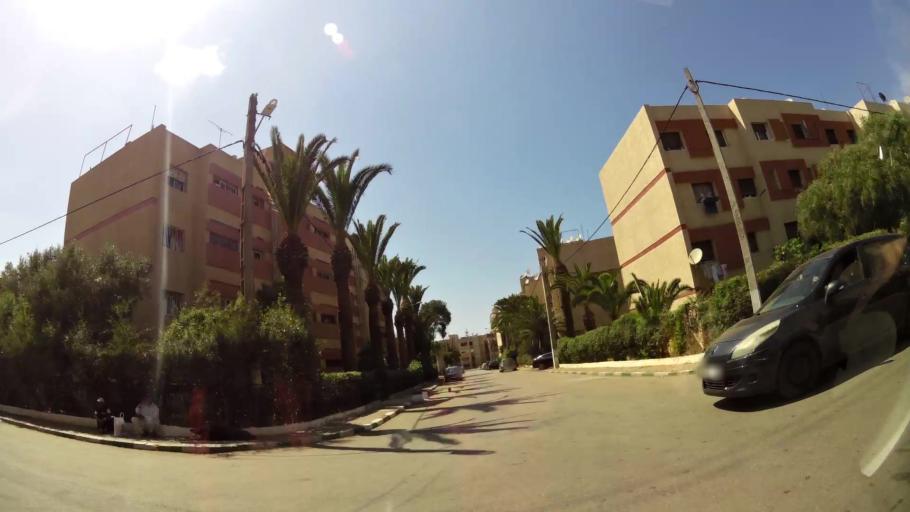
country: MA
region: Rabat-Sale-Zemmour-Zaer
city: Sale
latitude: 34.0419
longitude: -6.7898
